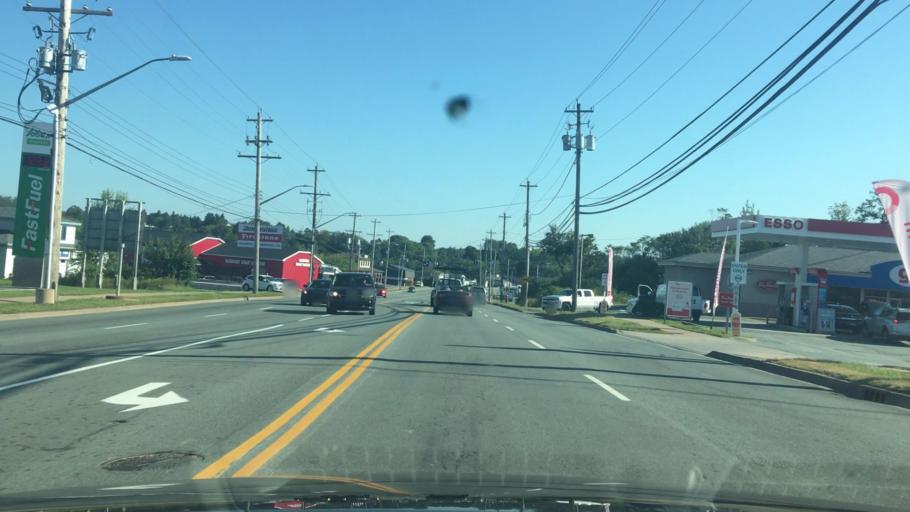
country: CA
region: Nova Scotia
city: Cole Harbour
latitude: 44.6949
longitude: -63.4972
